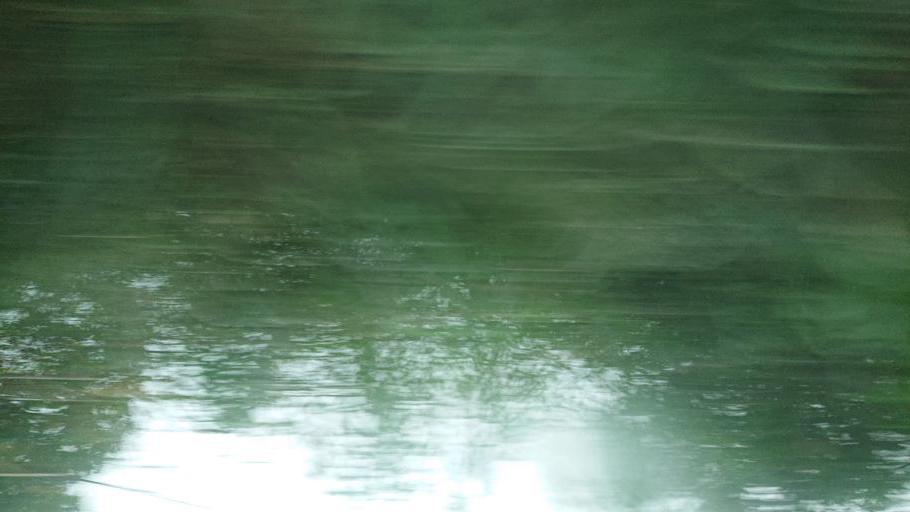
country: TW
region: Taiwan
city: Lugu
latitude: 23.5943
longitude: 120.7145
